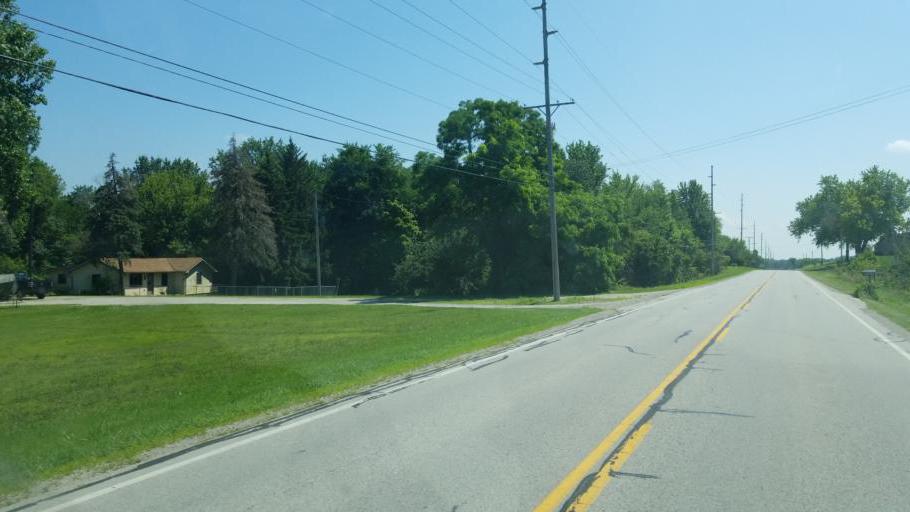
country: US
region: Ohio
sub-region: Huron County
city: Bellevue
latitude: 41.3673
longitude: -82.8256
